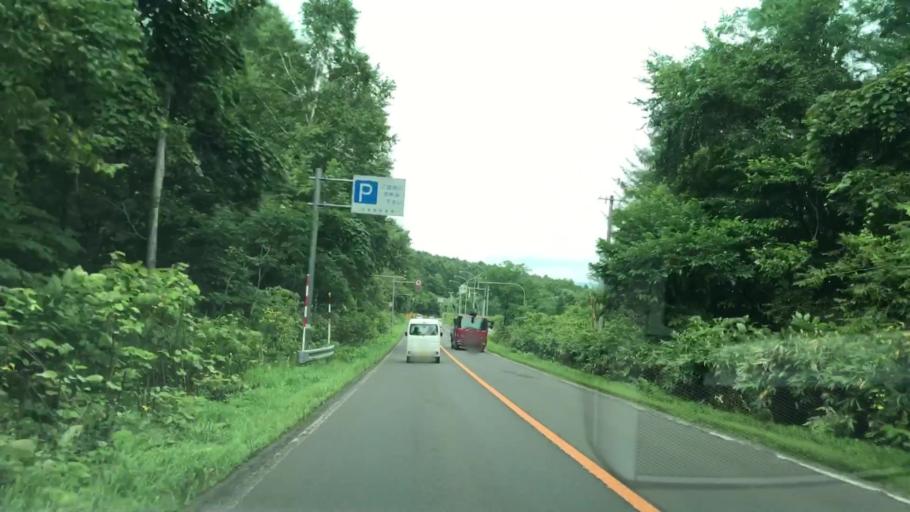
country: JP
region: Hokkaido
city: Niseko Town
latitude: 42.9492
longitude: 140.7013
